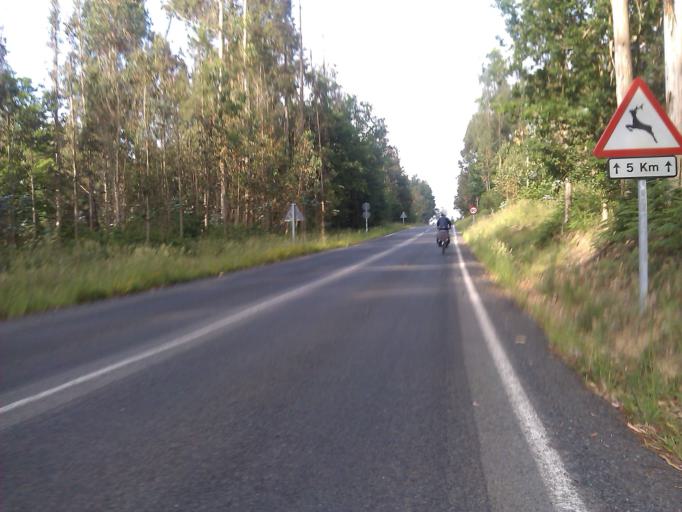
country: ES
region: Galicia
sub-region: Provincia da Coruna
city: Santiso
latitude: 42.8896
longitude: -8.0838
